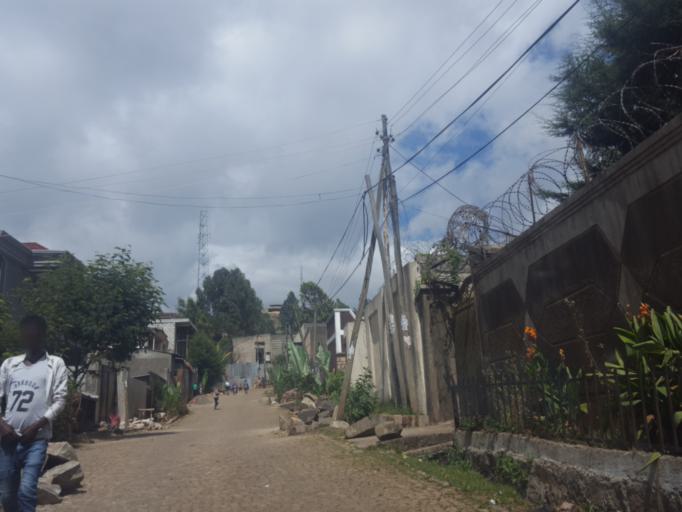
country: ET
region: Adis Abeba
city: Addis Ababa
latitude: 9.0668
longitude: 38.7295
